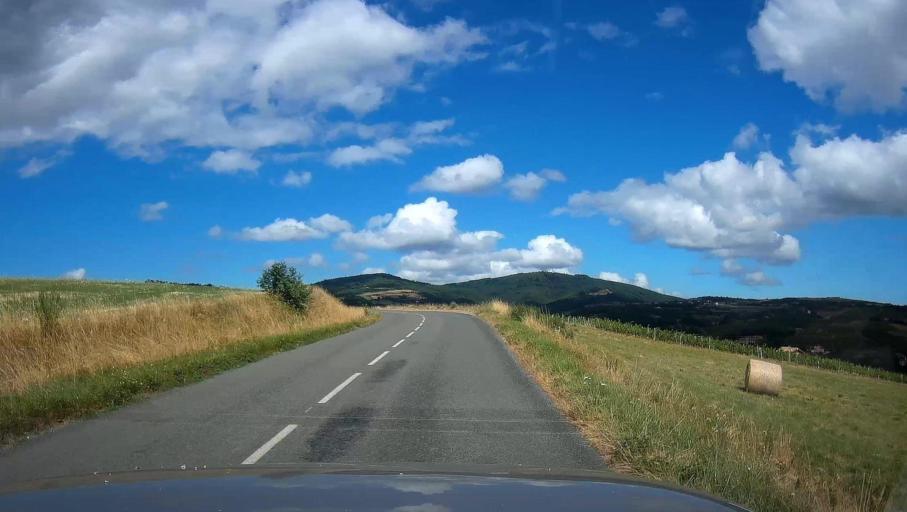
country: FR
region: Rhone-Alpes
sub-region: Departement du Rhone
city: Cogny
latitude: 45.9746
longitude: 4.6177
